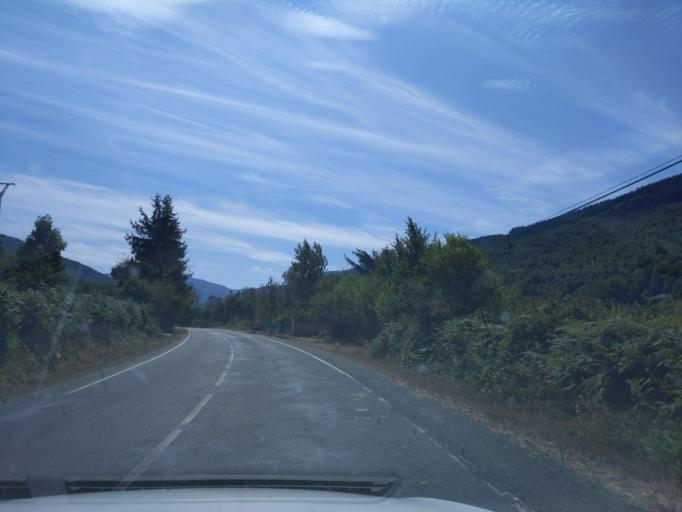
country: ES
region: La Rioja
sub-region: Provincia de La Rioja
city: Ezcaray
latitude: 42.3008
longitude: -3.0249
